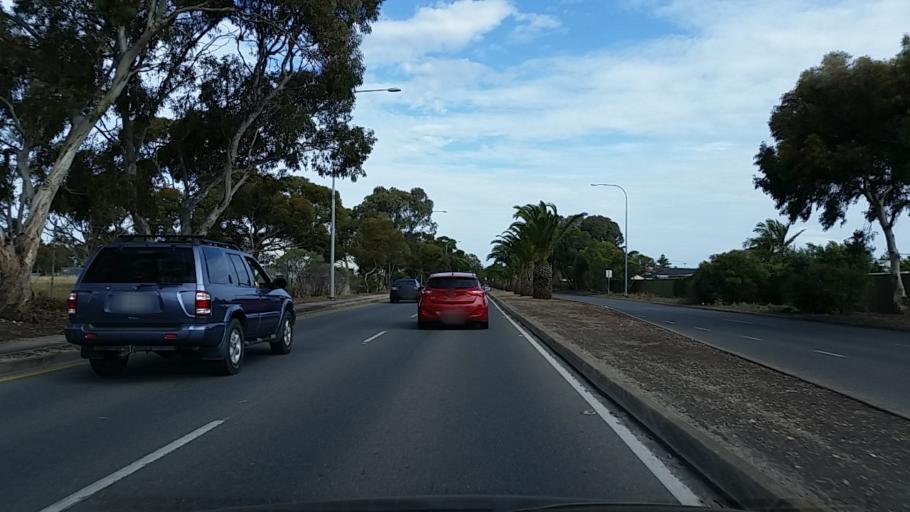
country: AU
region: South Australia
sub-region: Charles Sturt
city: Royal Park
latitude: -34.8804
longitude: 138.5158
